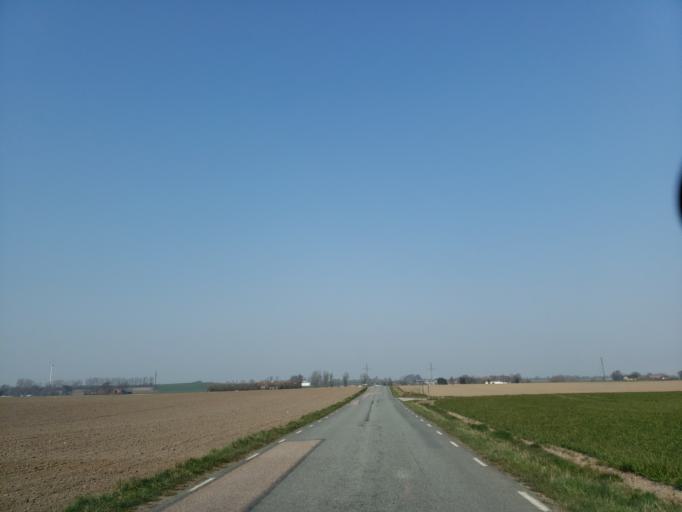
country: SE
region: Skane
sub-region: Simrishamns Kommun
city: Simrishamn
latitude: 55.4594
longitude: 14.2121
